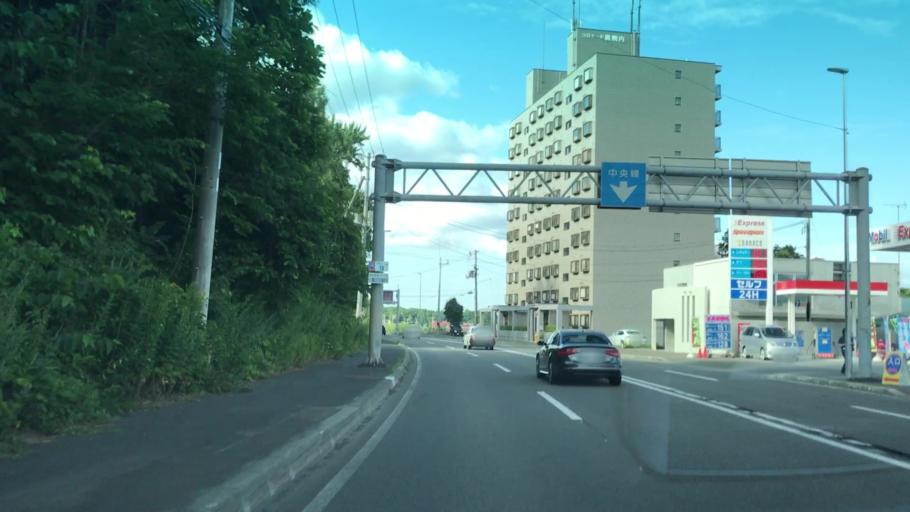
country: JP
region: Hokkaido
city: Sapporo
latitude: 42.9787
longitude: 141.3461
